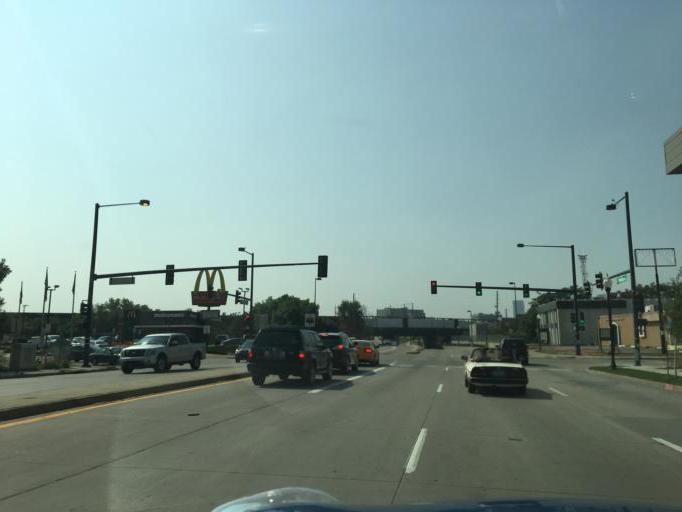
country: US
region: Colorado
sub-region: Denver County
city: Denver
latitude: 39.7789
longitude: -104.9793
